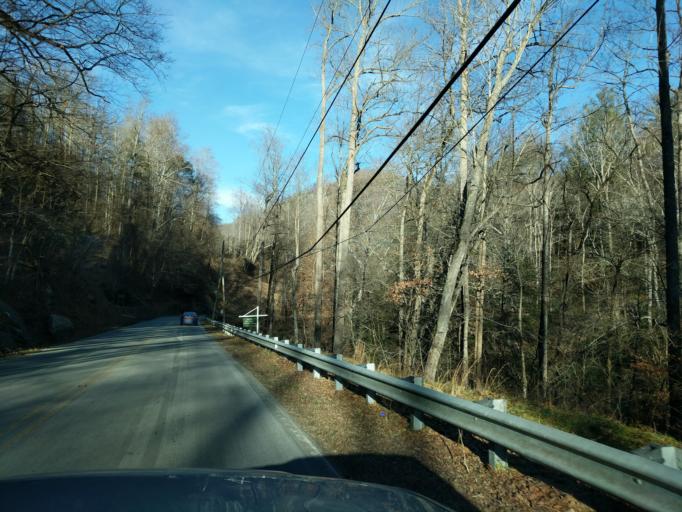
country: US
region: North Carolina
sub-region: Henderson County
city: Edneyville
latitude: 35.4481
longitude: -82.2915
